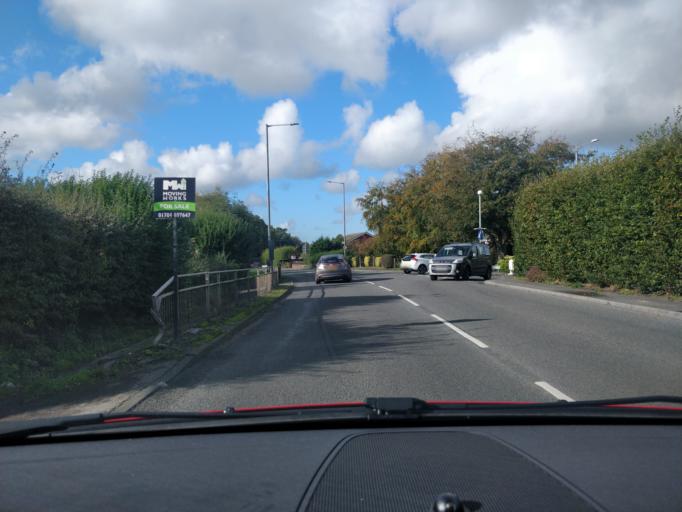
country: GB
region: England
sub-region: Lancashire
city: Parbold
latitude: 53.5907
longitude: -2.8208
